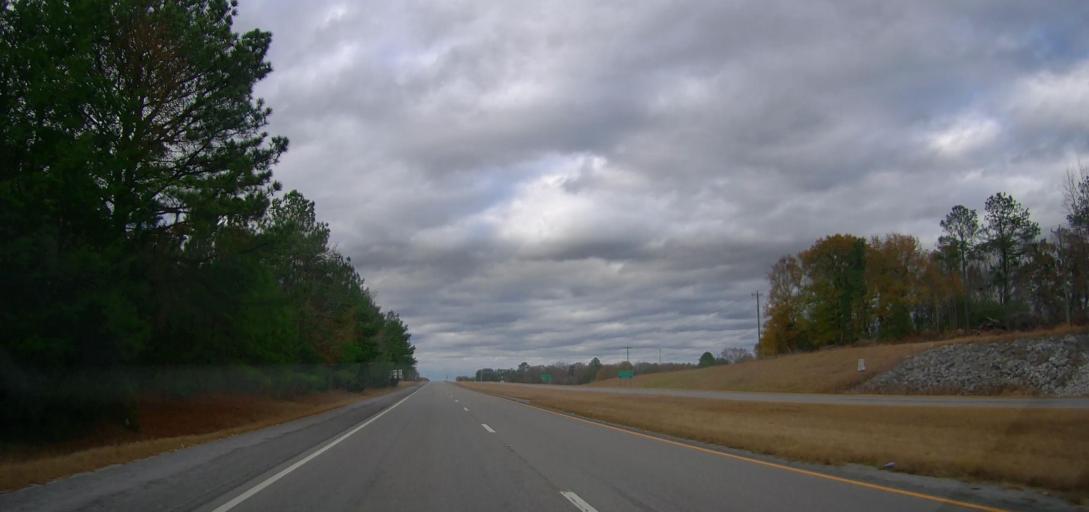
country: US
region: Alabama
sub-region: Lawrence County
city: Moulton
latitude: 34.5171
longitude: -87.2929
